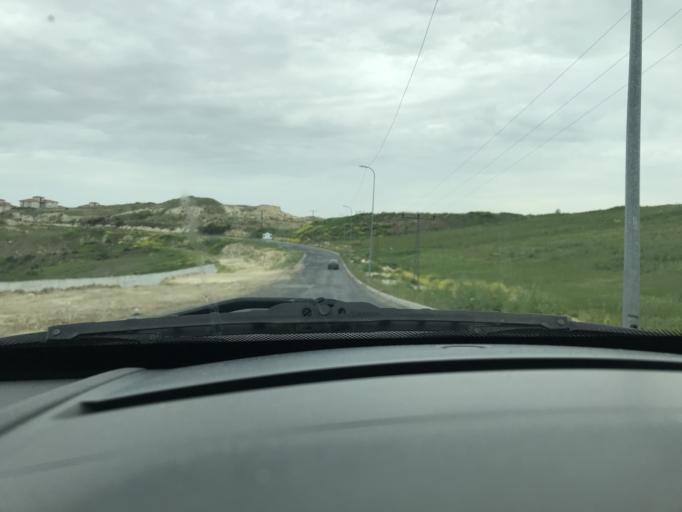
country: TR
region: Istanbul
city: Esenyurt
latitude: 41.0959
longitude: 28.6808
